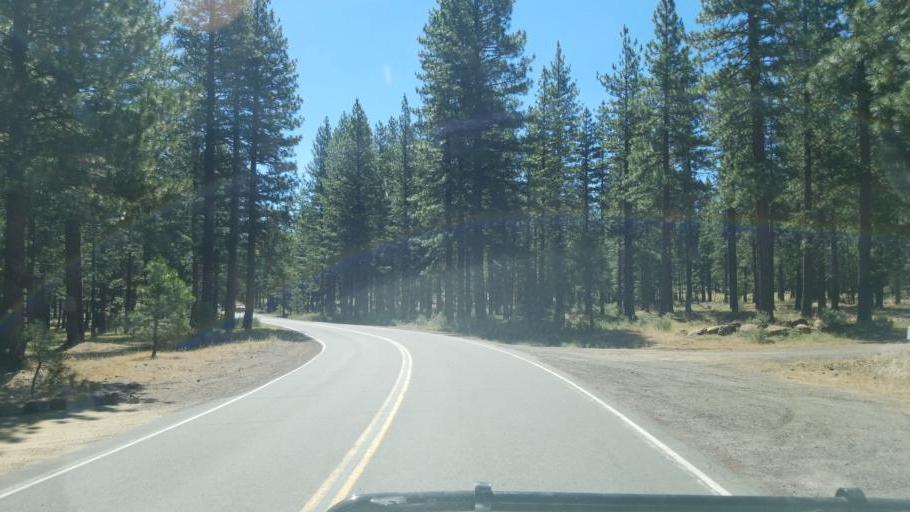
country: US
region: California
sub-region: Lassen County
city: Susanville
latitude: 40.4231
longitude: -120.7207
